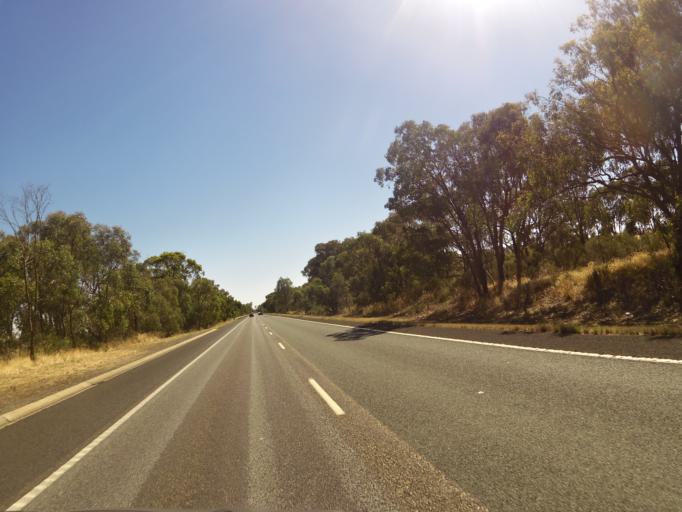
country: AU
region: Victoria
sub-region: Greater Shepparton
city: Shepparton
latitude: -36.8879
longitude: 145.2632
